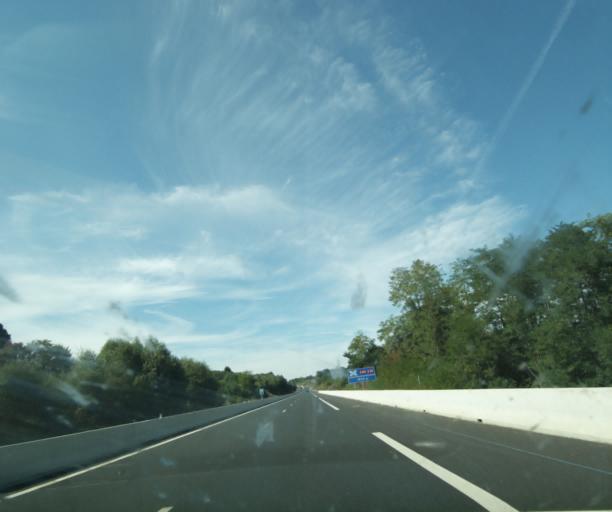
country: FR
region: Limousin
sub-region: Departement de la Correze
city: Saint-Mexant
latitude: 45.2962
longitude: 1.5938
